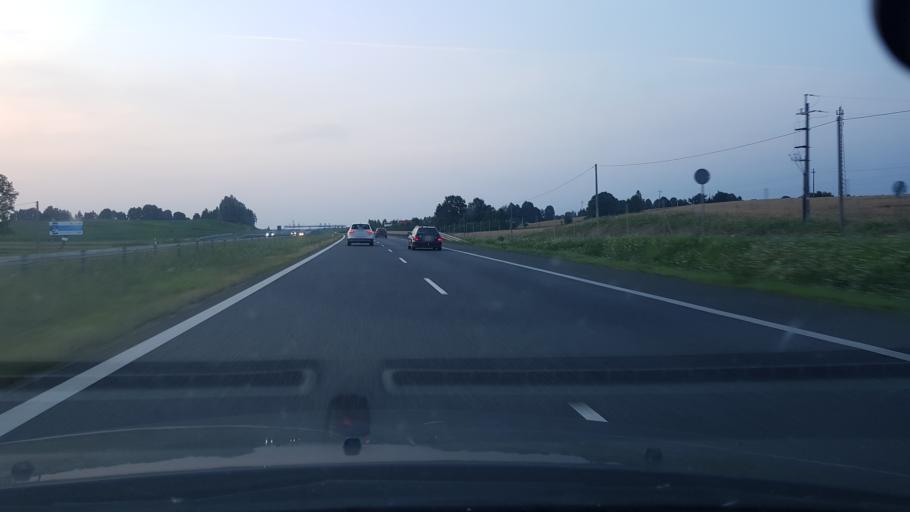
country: PL
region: Warmian-Masurian Voivodeship
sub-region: Powiat olsztynski
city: Olsztynek
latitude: 53.4816
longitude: 20.3213
